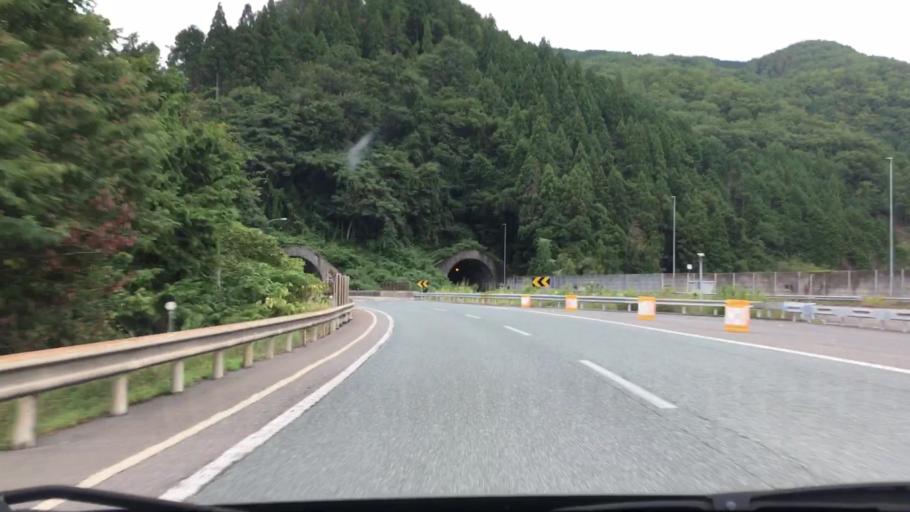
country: JP
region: Okayama
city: Niimi
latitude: 35.0077
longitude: 133.4806
